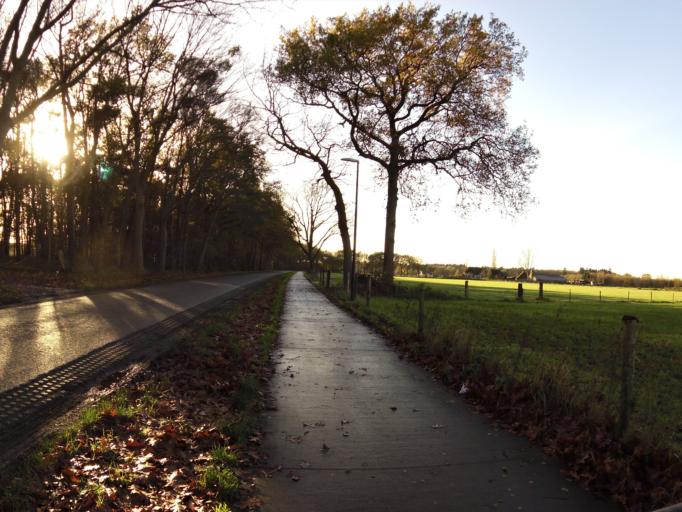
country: NL
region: North Brabant
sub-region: Gemeente Haaren
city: Haaren
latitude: 51.6497
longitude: 5.2266
